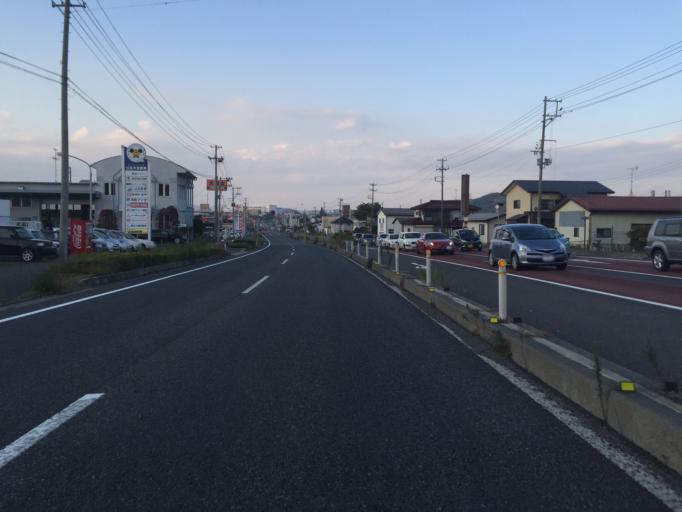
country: JP
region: Fukushima
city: Motomiya
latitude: 37.5098
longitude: 140.3952
